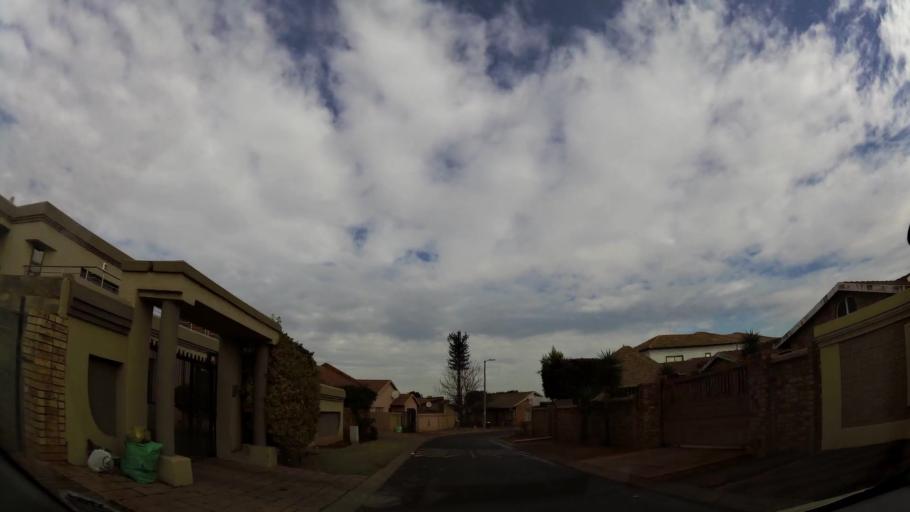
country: ZA
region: Gauteng
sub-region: Ekurhuleni Metropolitan Municipality
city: Germiston
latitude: -26.3238
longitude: 28.1814
